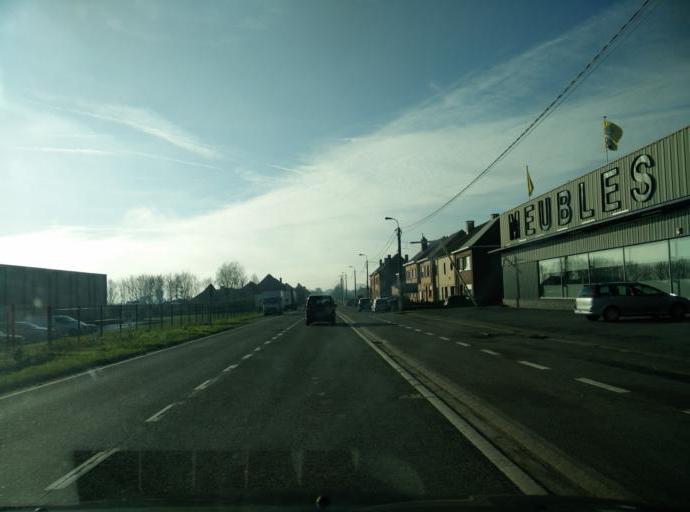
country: BE
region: Wallonia
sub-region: Province du Brabant Wallon
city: Tubize
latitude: 50.7104
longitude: 4.1697
